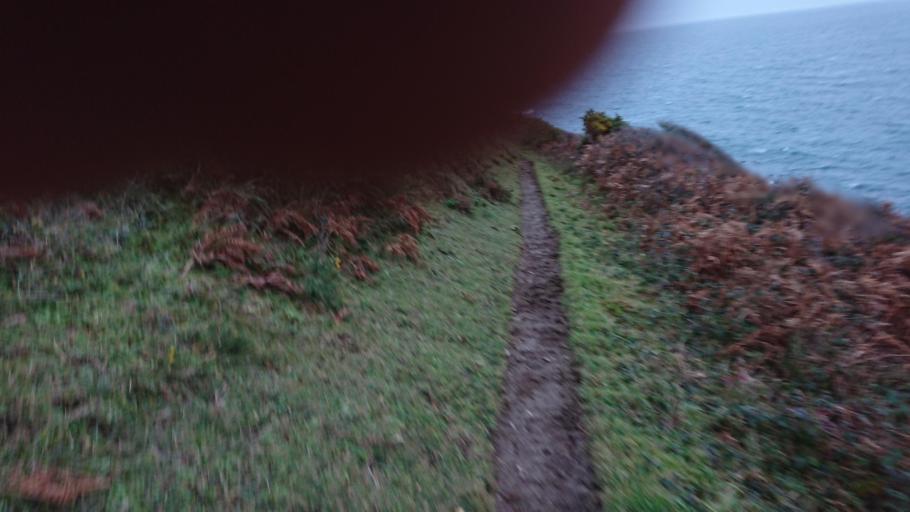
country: GB
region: England
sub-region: Cornwall
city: Fowey
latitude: 50.3293
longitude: -4.5673
